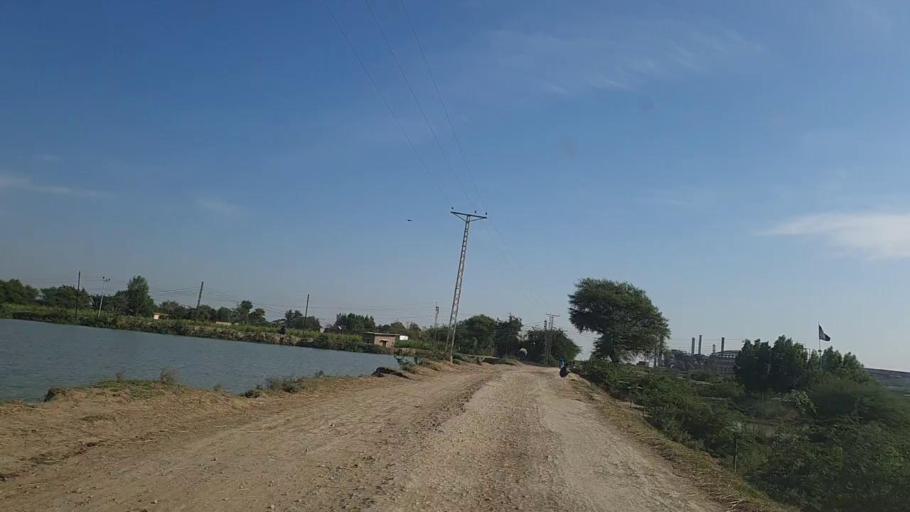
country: PK
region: Sindh
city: Bulri
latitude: 24.8121
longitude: 68.3223
